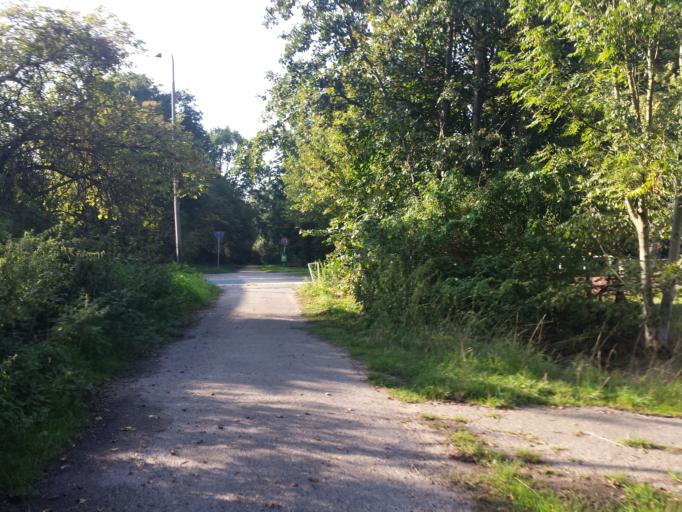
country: DE
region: Bremen
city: Bremen
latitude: 53.0352
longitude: 8.8522
